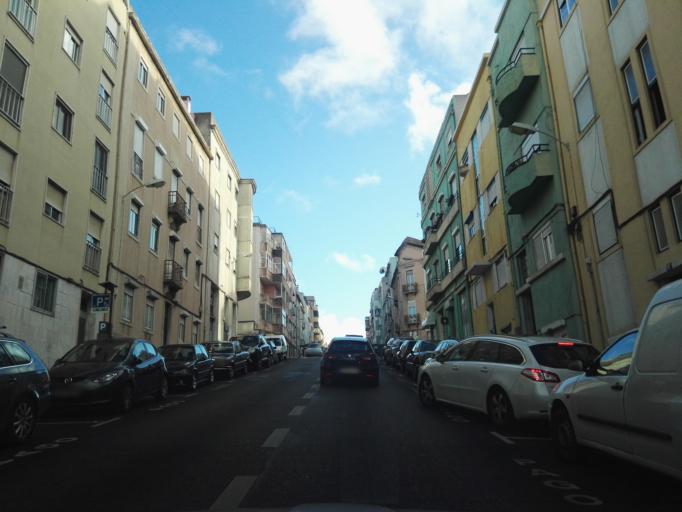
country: PT
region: Lisbon
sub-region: Lisbon
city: Lisbon
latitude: 38.7197
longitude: -9.1696
